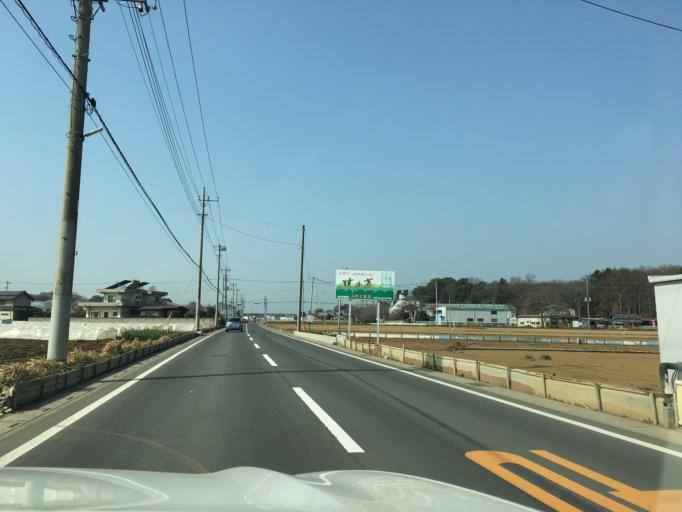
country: JP
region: Saitama
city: Kamifukuoka
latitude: 35.8612
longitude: 139.4872
